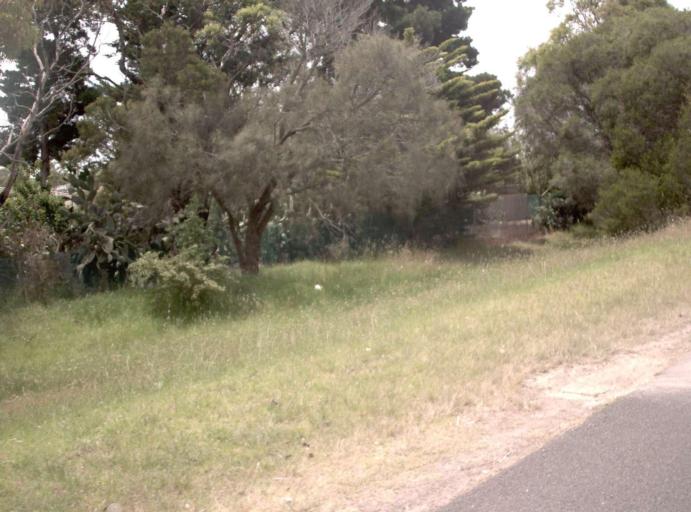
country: AU
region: Victoria
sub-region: Mornington Peninsula
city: McCrae
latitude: -38.3590
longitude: 144.9222
